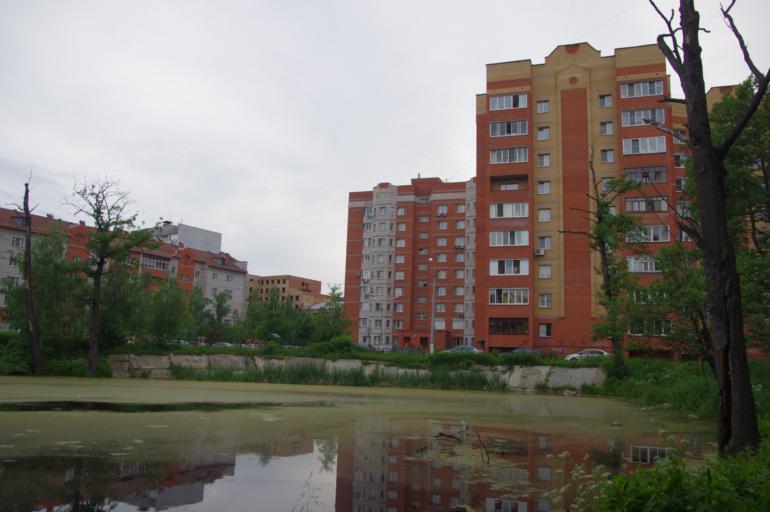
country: RU
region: Moskovskaya
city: Ramenskoye
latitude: 55.5744
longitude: 38.2346
